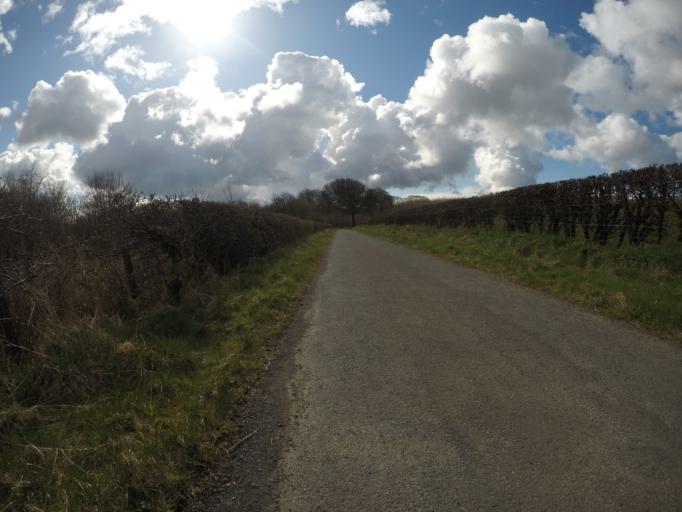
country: GB
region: Scotland
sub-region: North Ayrshire
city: Kilbirnie
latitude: 55.7288
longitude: -4.6696
